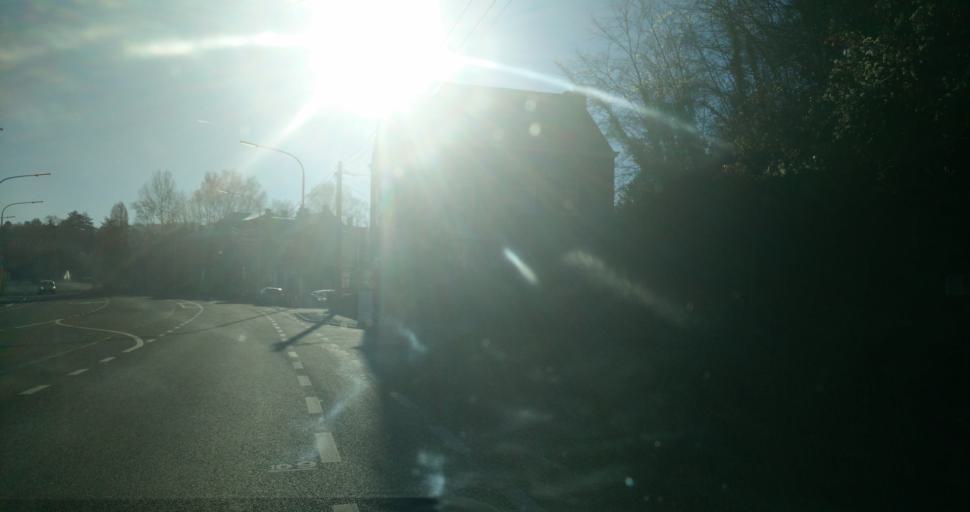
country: BE
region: Wallonia
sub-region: Province de Namur
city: Profondeville
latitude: 50.3800
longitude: 4.8664
